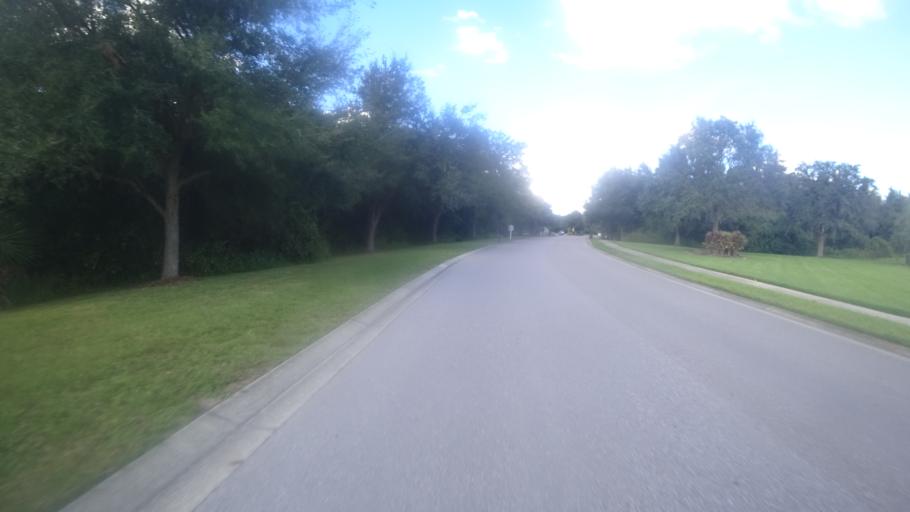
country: US
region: Florida
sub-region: Manatee County
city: Ellenton
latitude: 27.5508
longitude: -82.3866
